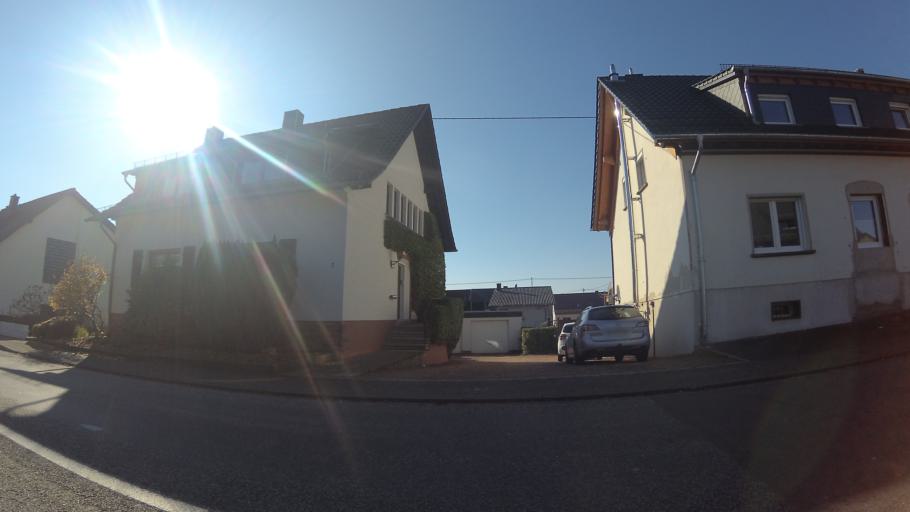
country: DE
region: Saarland
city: Weiskirchen
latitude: 49.5540
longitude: 6.8180
